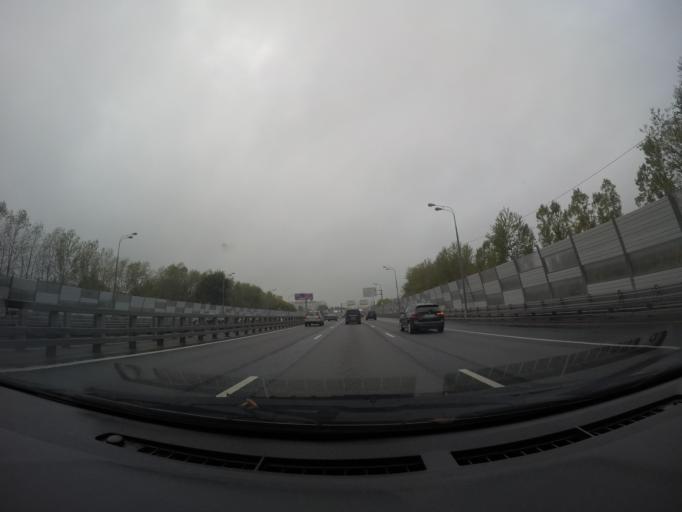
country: RU
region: Moscow
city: Shchukino
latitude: 55.7727
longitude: 37.4294
